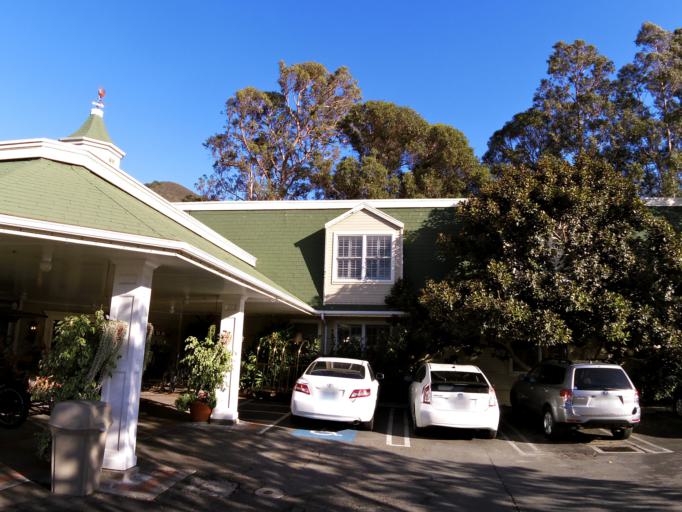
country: US
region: California
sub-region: San Luis Obispo County
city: San Luis Obispo
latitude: 35.2902
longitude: -120.6489
